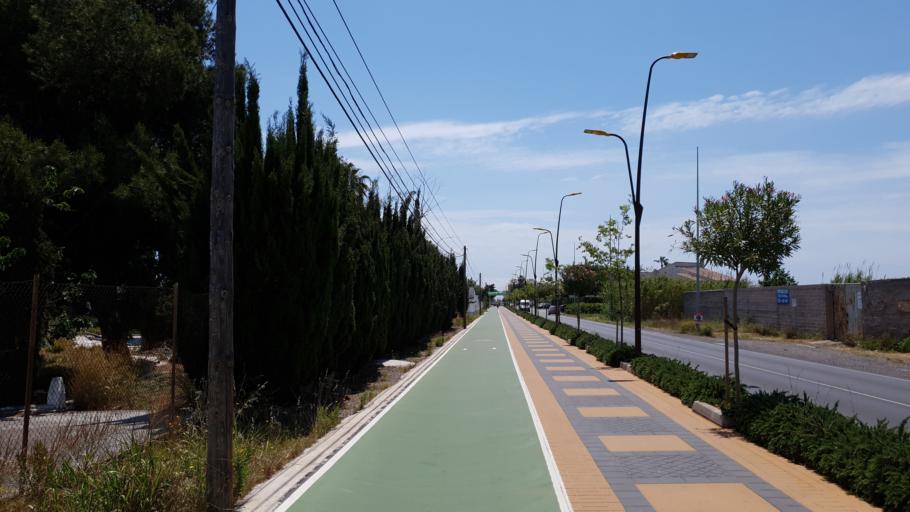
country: ES
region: Valencia
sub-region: Provincia de Castello
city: Burriana
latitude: 39.8741
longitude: -0.0760
